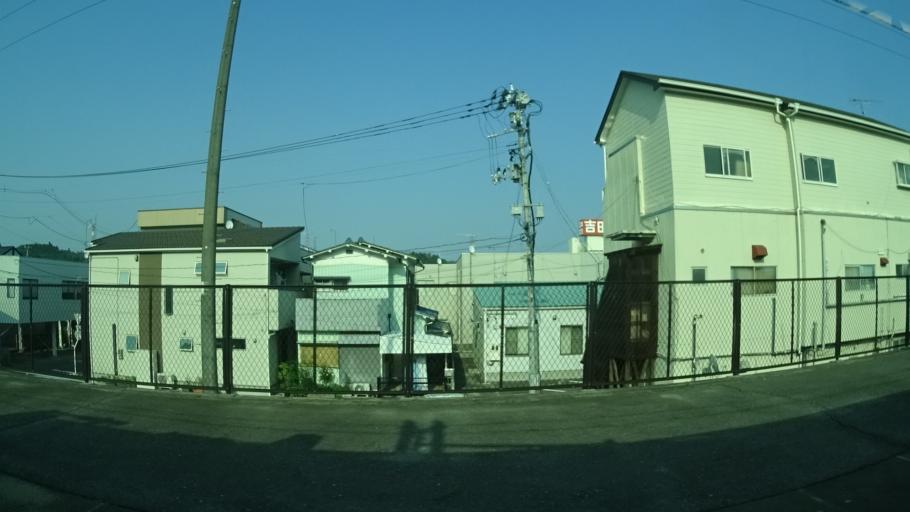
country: JP
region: Ibaraki
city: Kitaibaraki
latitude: 36.9213
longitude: 140.7967
